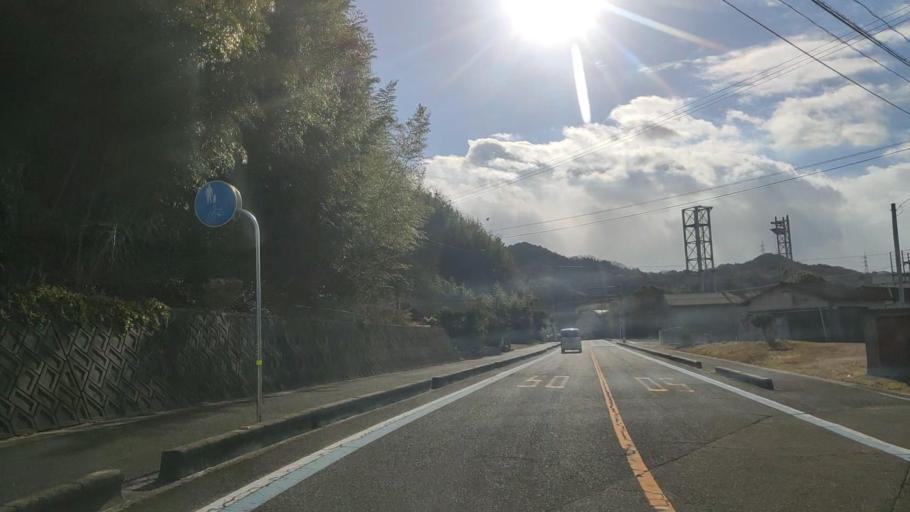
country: JP
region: Hiroshima
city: Innoshima
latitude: 34.2201
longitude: 133.0685
